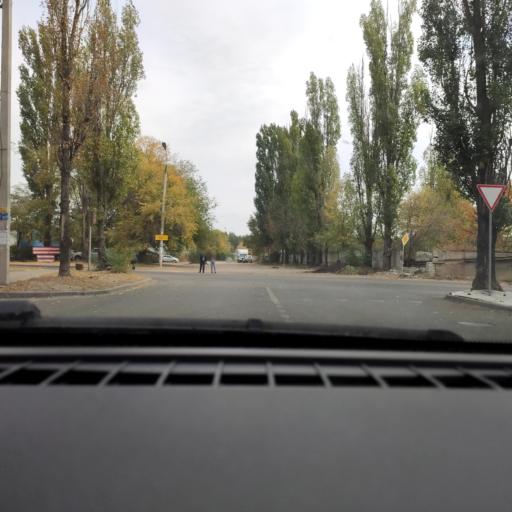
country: RU
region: Voronezj
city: Voronezh
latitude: 51.6795
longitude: 39.2697
